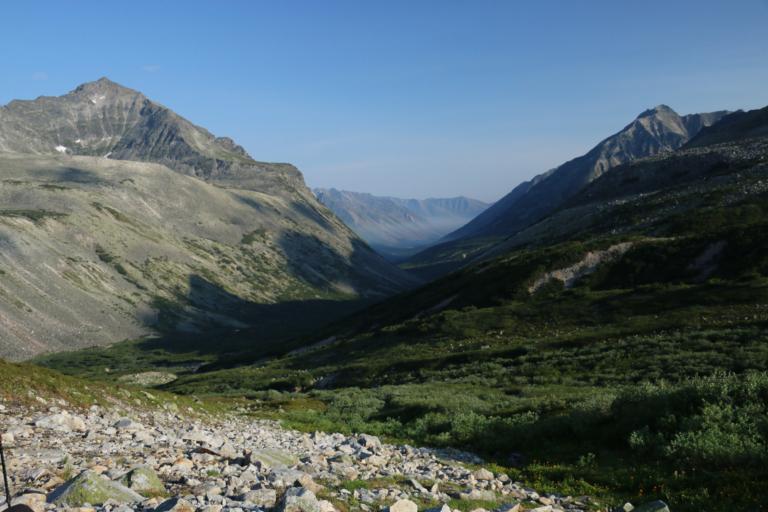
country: RU
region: Respublika Buryatiya
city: Novyy Uoyan
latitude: 56.2276
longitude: 110.9544
